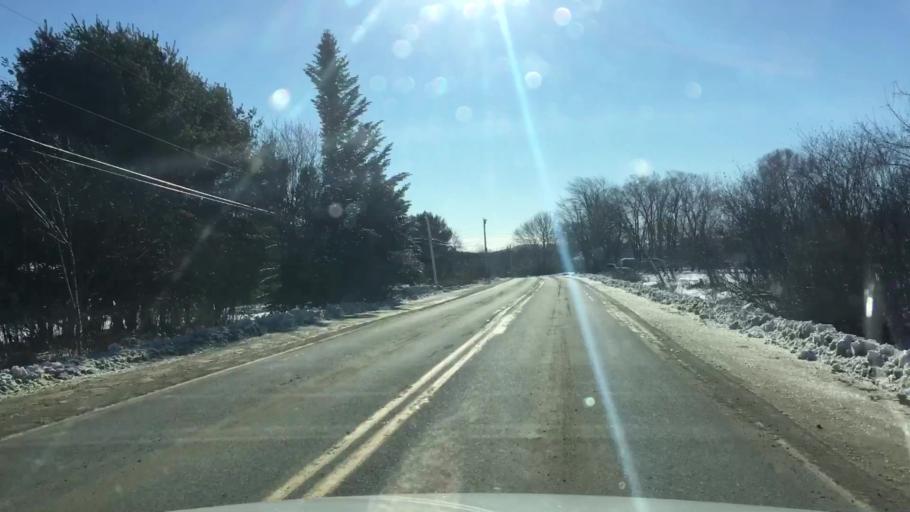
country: US
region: Maine
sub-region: Kennebec County
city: Readfield
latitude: 44.3629
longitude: -69.9895
